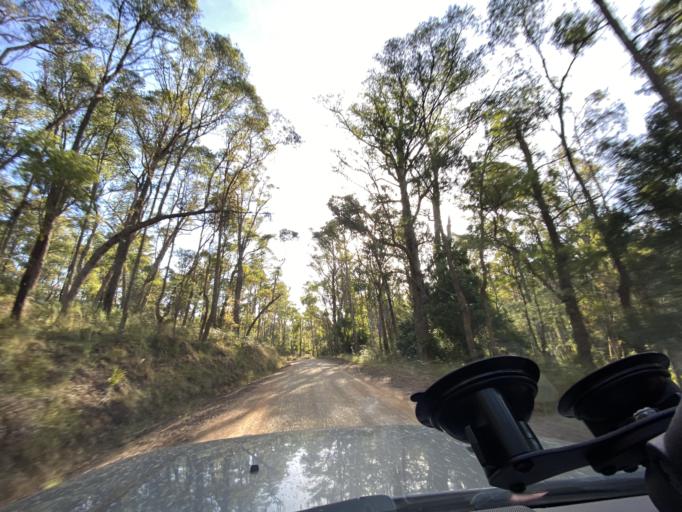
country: AU
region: Victoria
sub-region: Mansfield
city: Mansfield
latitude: -37.5191
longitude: 146.0632
